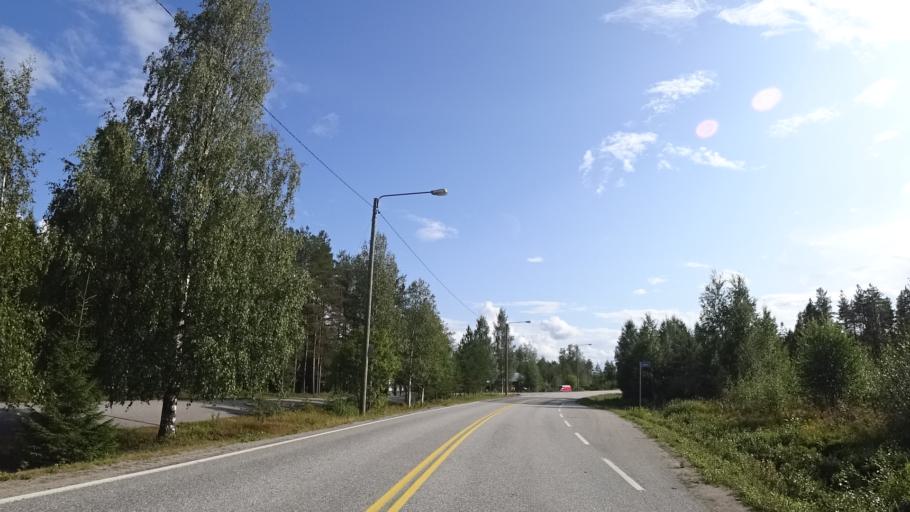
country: FI
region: North Karelia
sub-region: Pielisen Karjala
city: Lieksa
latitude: 63.4202
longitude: 30.1049
